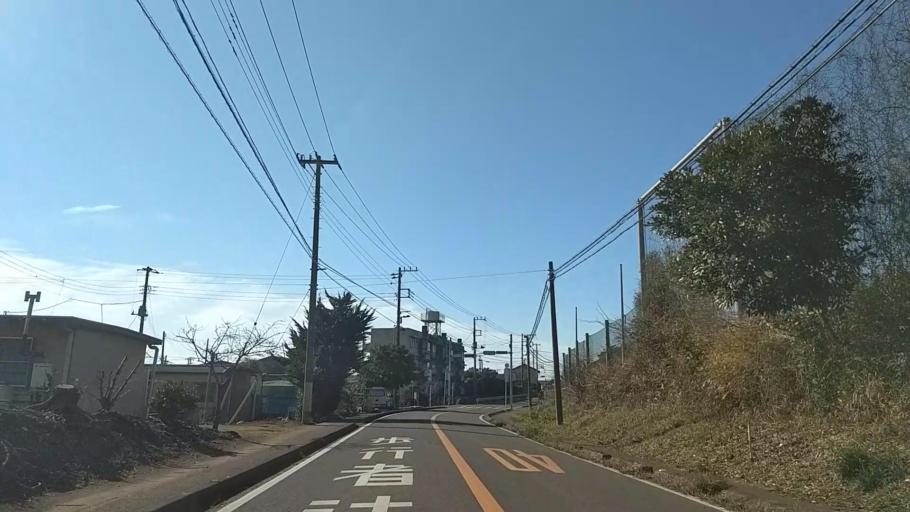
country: JP
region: Chiba
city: Hasaki
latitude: 35.7018
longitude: 140.8586
